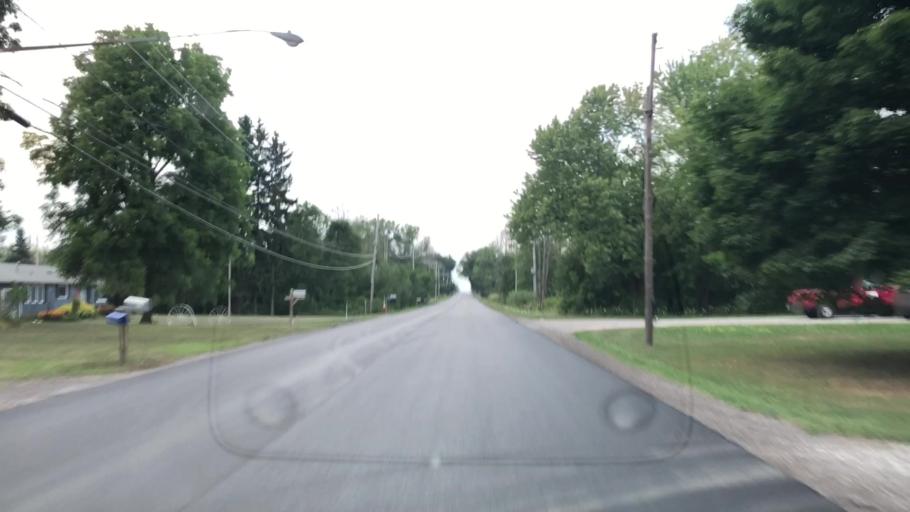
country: US
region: New York
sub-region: Erie County
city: Billington Heights
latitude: 42.8110
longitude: -78.6059
